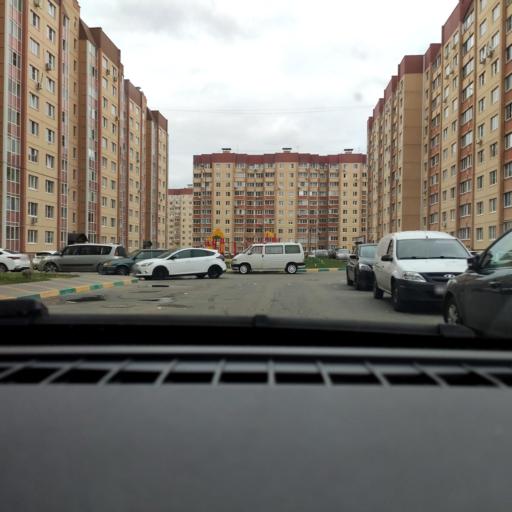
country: RU
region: Voronezj
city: Voronezh
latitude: 51.7166
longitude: 39.2647
